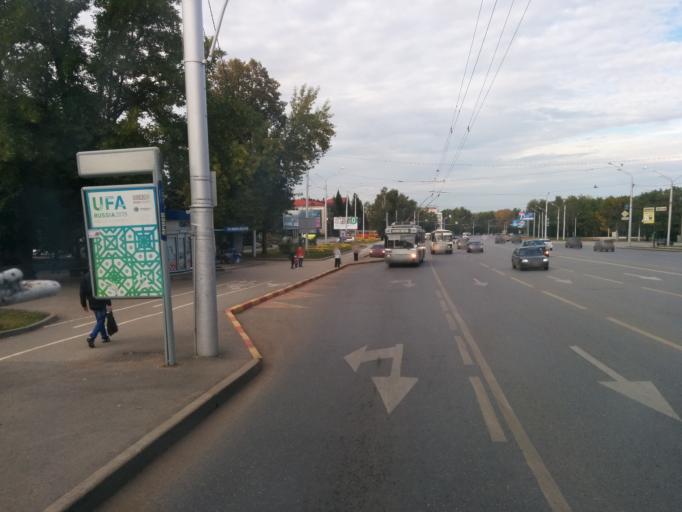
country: RU
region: Bashkortostan
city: Ufa
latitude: 54.7949
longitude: 56.0381
